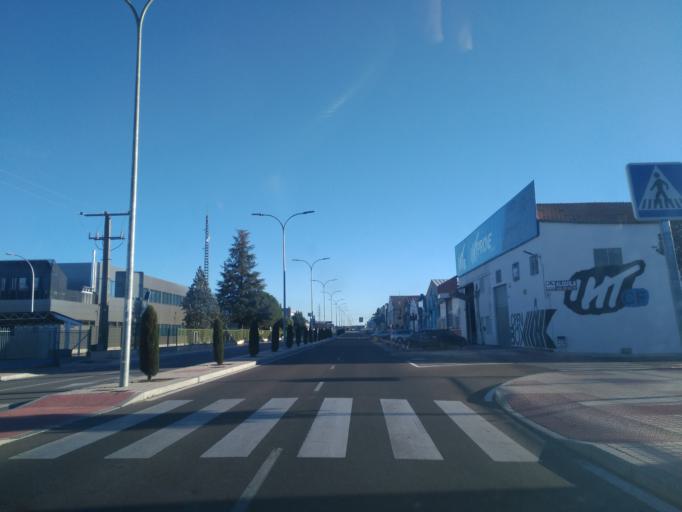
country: ES
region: Castille and Leon
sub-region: Provincia de Salamanca
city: Carbajosa de la Sagrada
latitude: 40.9472
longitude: -5.6563
